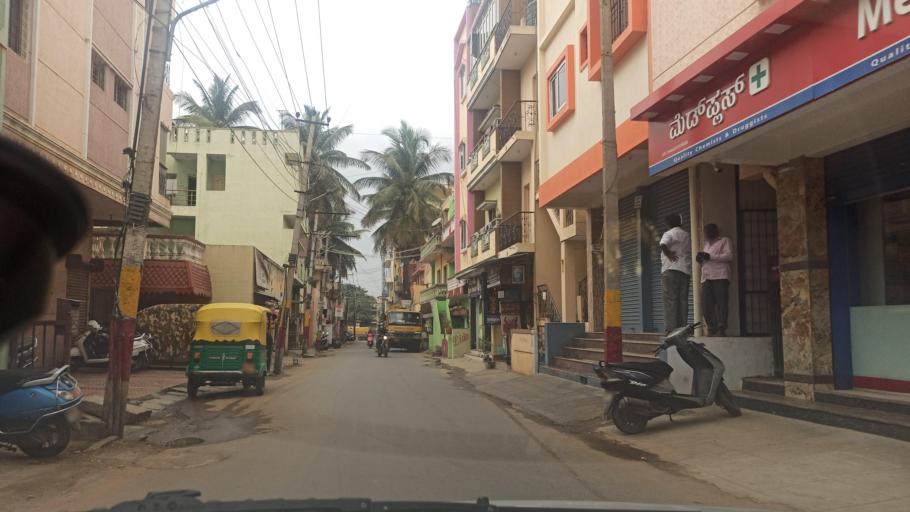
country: IN
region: Karnataka
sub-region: Bangalore Urban
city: Yelahanka
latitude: 13.0373
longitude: 77.5907
